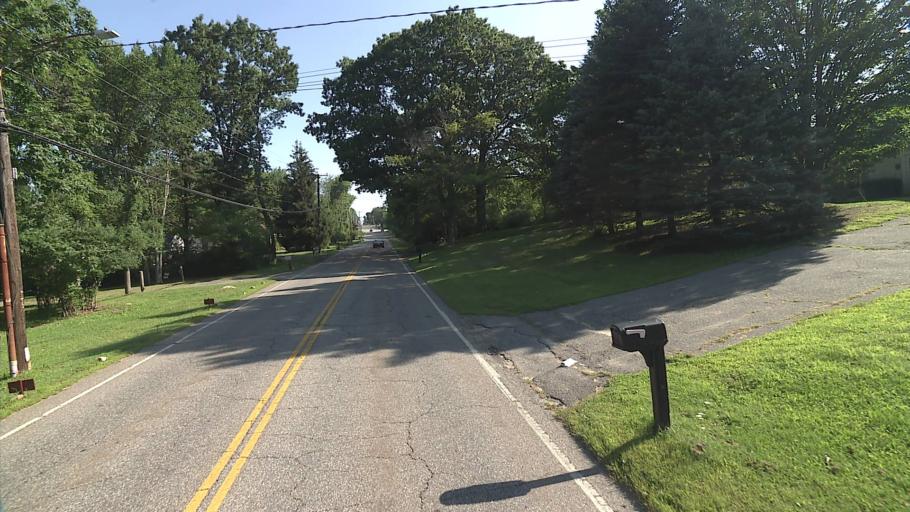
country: US
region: Connecticut
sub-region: Litchfield County
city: Northwest Harwinton
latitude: 41.8167
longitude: -73.0822
